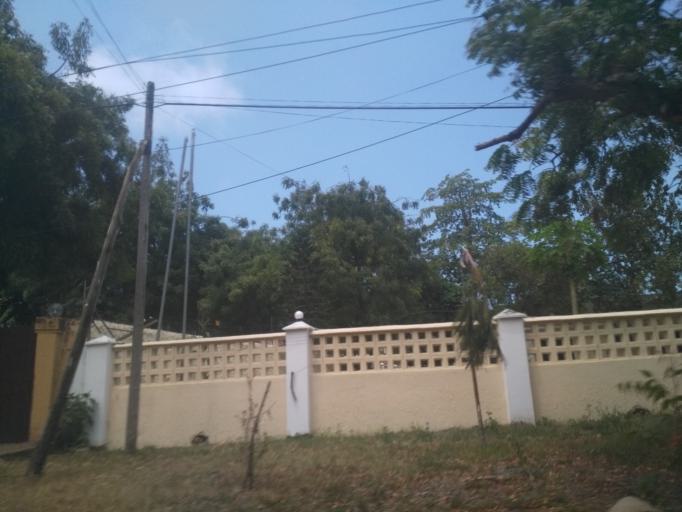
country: TZ
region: Dar es Salaam
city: Magomeni
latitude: -6.7496
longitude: 39.2770
